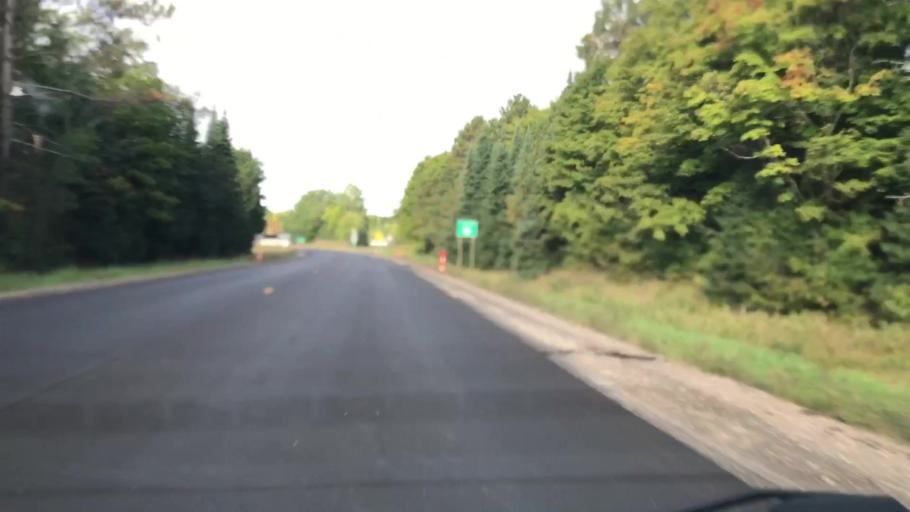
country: US
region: Michigan
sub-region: Luce County
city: Newberry
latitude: 46.3464
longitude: -85.0243
